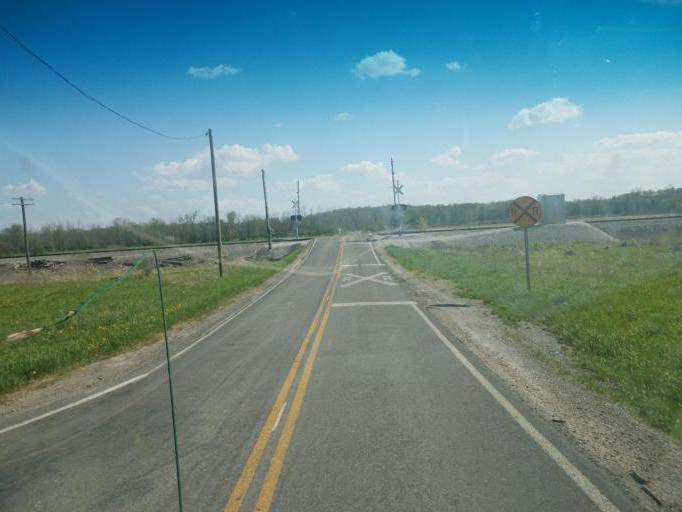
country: US
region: Ohio
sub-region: Medina County
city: Westfield Center
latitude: 40.9950
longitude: -81.9412
